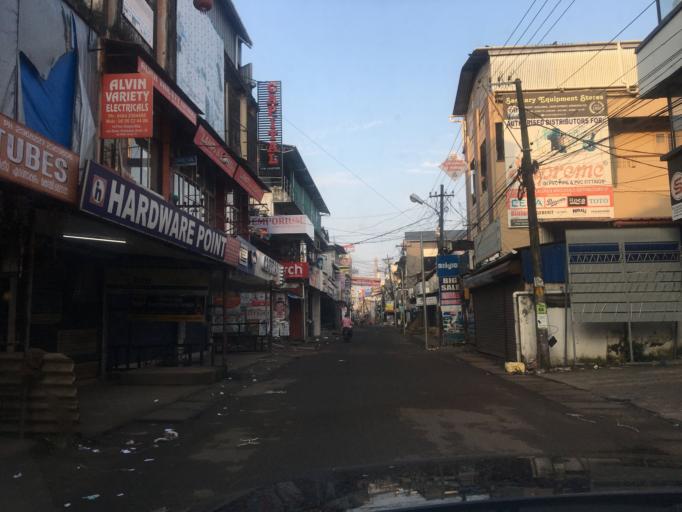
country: IN
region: Kerala
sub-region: Ernakulam
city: Cochin
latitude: 9.9810
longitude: 76.2802
